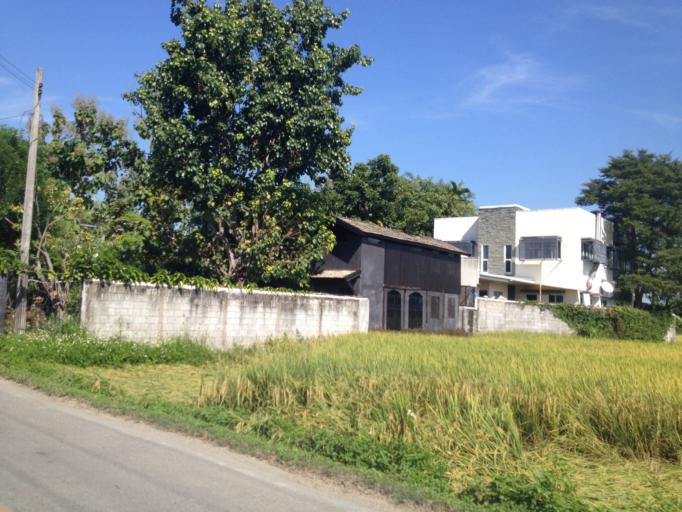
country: TH
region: Chiang Mai
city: Hang Dong
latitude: 18.7066
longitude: 98.9660
